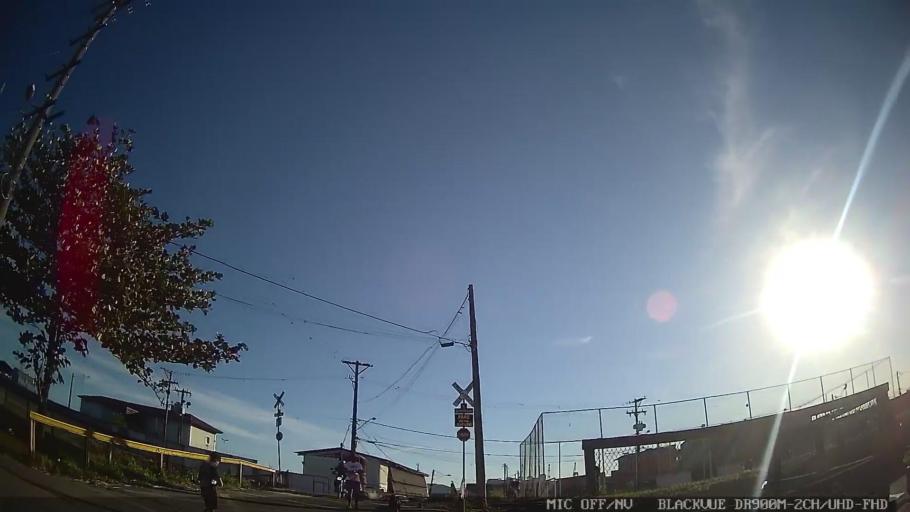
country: BR
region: Sao Paulo
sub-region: Santos
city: Santos
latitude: -23.9462
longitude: -46.3059
